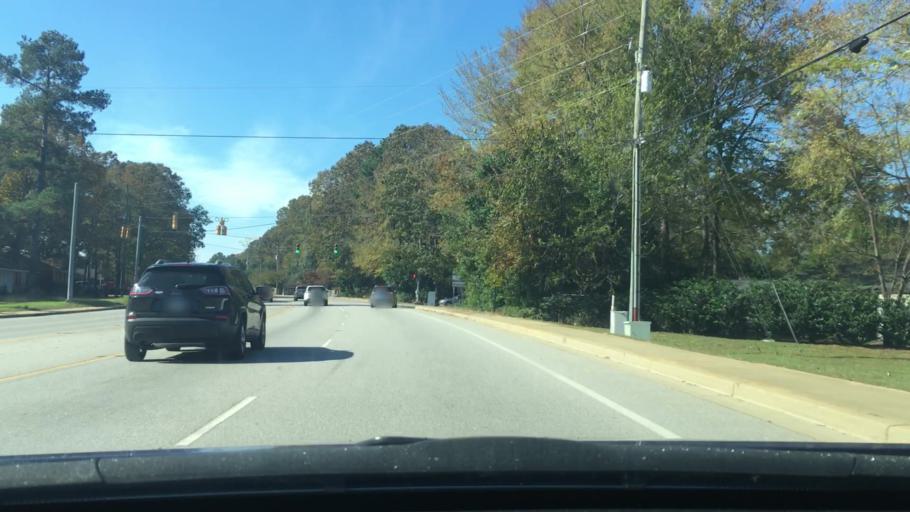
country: US
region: South Carolina
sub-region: Sumter County
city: South Sumter
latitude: 33.9034
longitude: -80.3876
